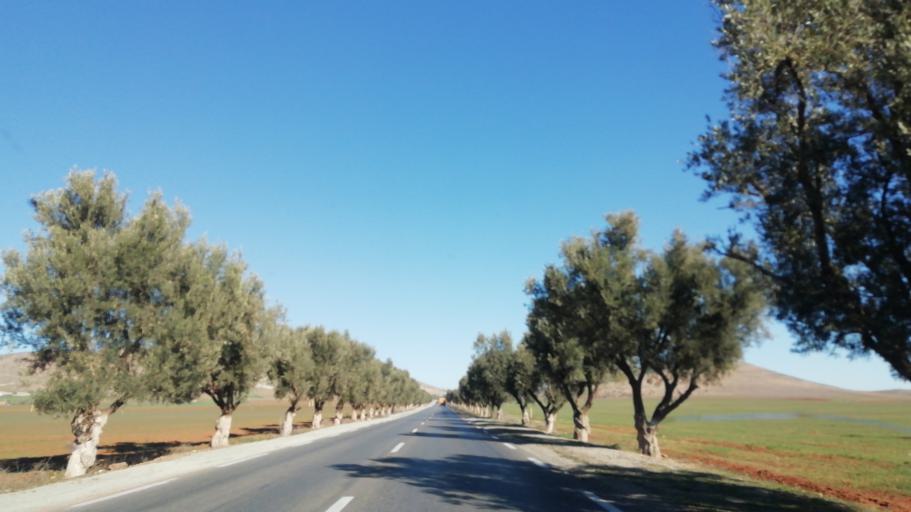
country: DZ
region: Mascara
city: Mascara
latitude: 35.2275
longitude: 0.1147
